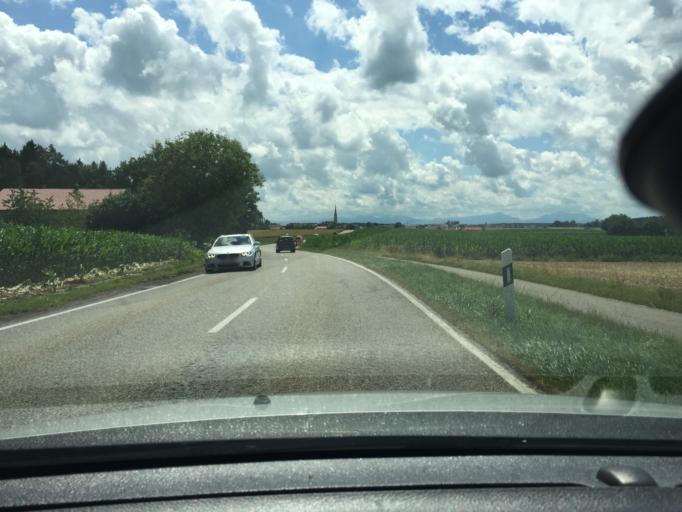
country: DE
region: Bavaria
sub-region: Upper Bavaria
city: Kienberg
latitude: 48.0835
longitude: 12.4806
